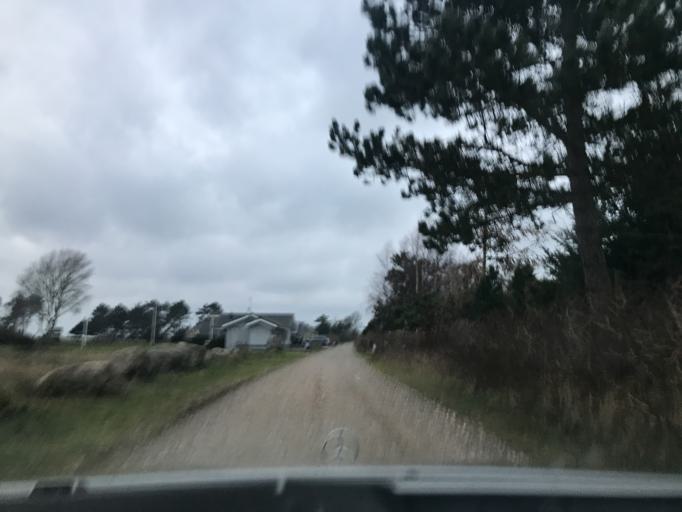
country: DK
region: South Denmark
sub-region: Sonderborg Kommune
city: Horuphav
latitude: 54.8588
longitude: 9.9242
